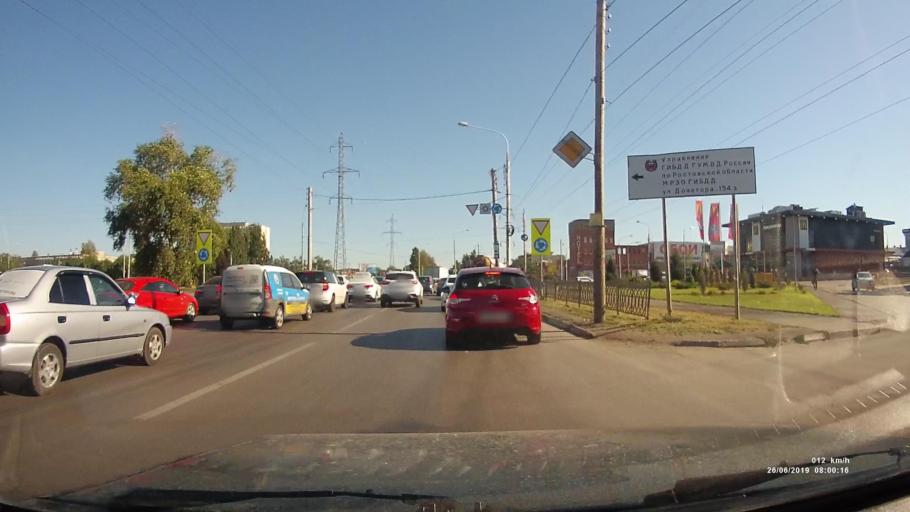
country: RU
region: Rostov
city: Kalinin
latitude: 47.2365
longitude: 39.6140
